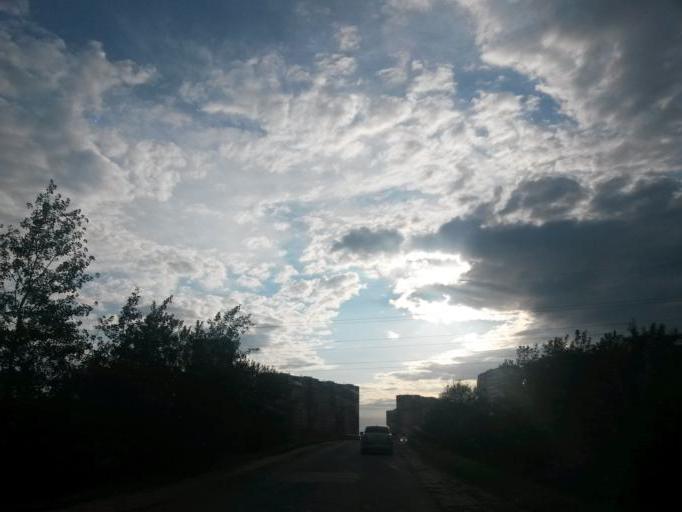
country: RU
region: Moskovskaya
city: Vostryakovo
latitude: 55.3962
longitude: 37.7798
